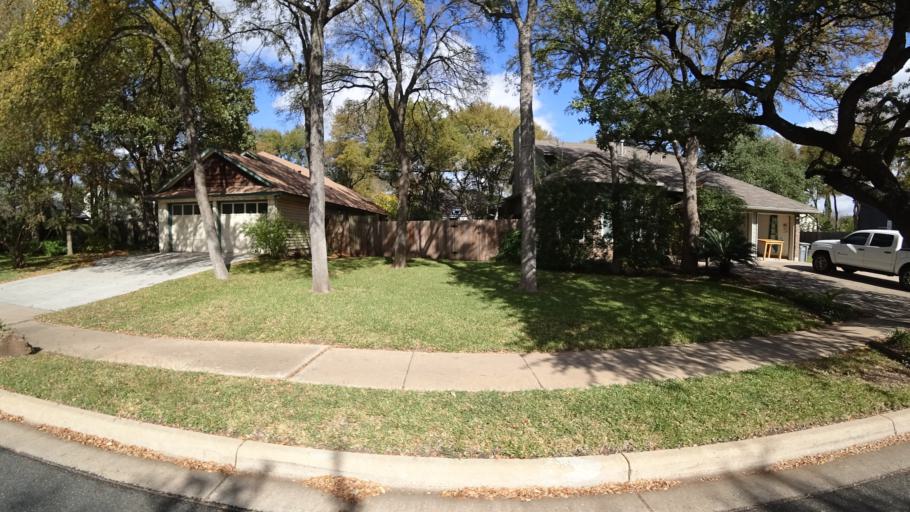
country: US
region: Texas
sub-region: Travis County
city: Wells Branch
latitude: 30.4254
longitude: -97.7205
